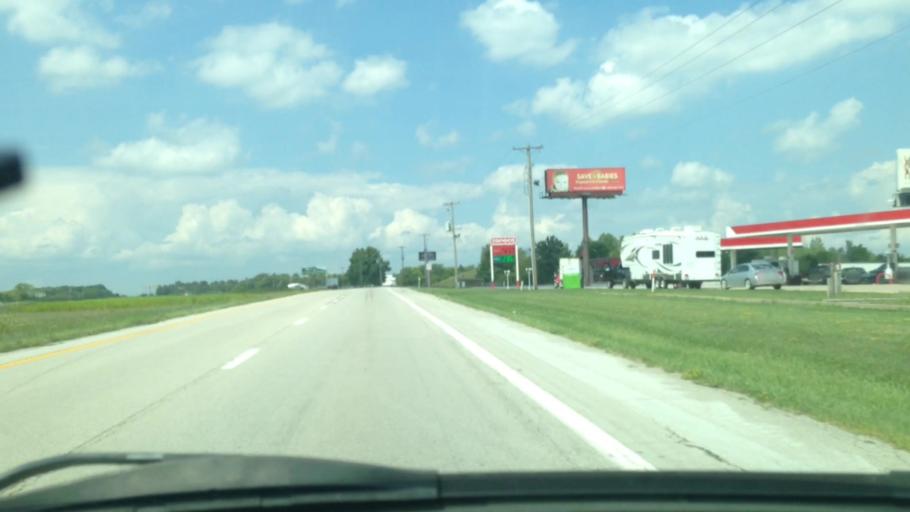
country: US
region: Missouri
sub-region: Lincoln County
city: Troy
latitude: 39.1348
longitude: -90.9643
